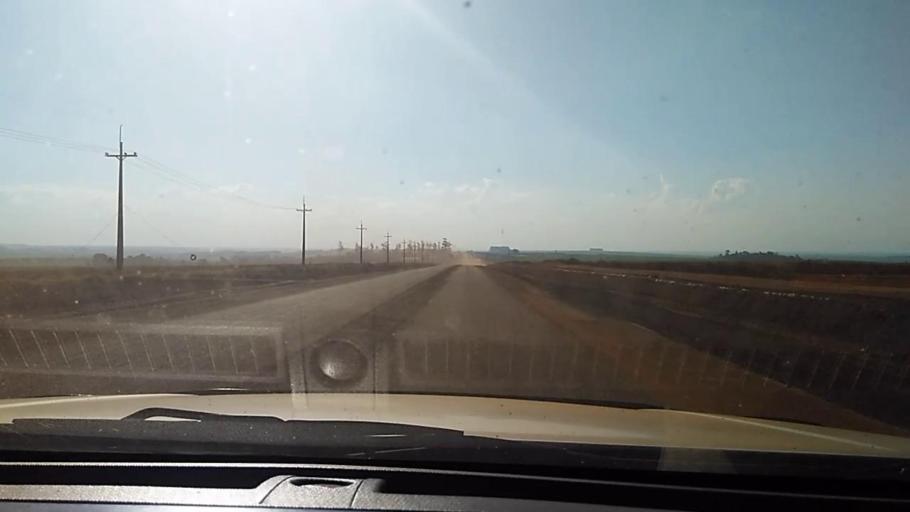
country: PY
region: Alto Parana
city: Naranjal
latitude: -25.9151
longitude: -55.4378
